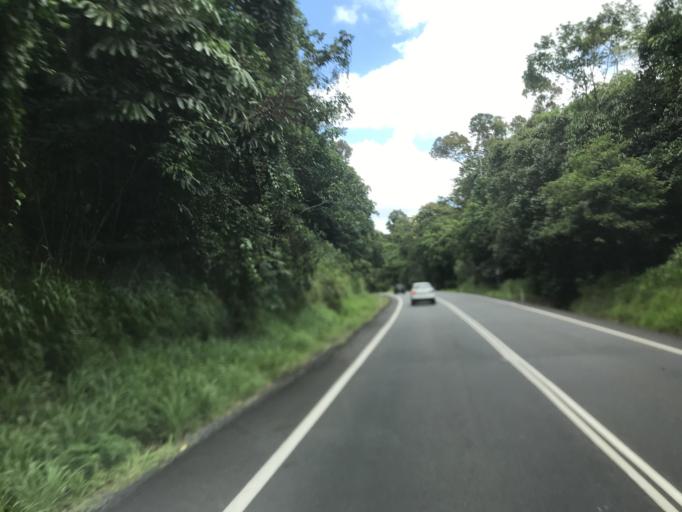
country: AU
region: Queensland
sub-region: Cassowary Coast
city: Innisfail
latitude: -17.6057
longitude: 145.7693
